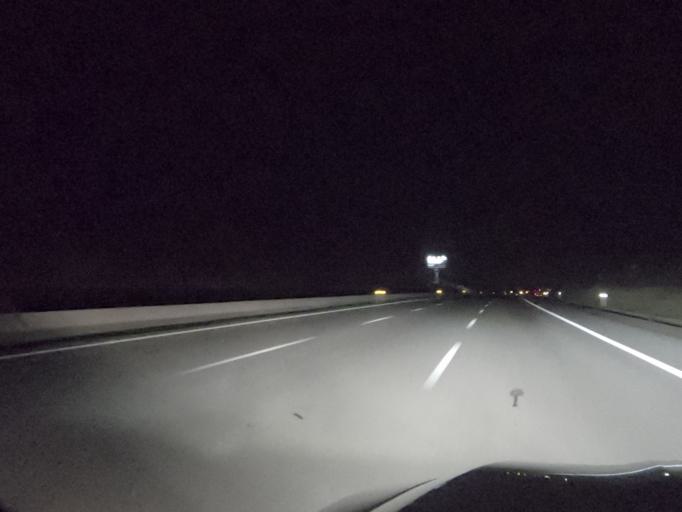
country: PT
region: Santarem
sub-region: Alpiarca
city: Alpiarca
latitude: 39.3390
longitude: -8.6539
